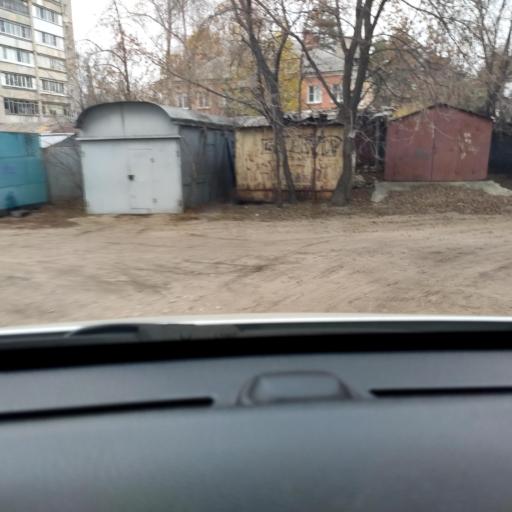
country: RU
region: Voronezj
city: Voronezh
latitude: 51.7239
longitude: 39.2605
